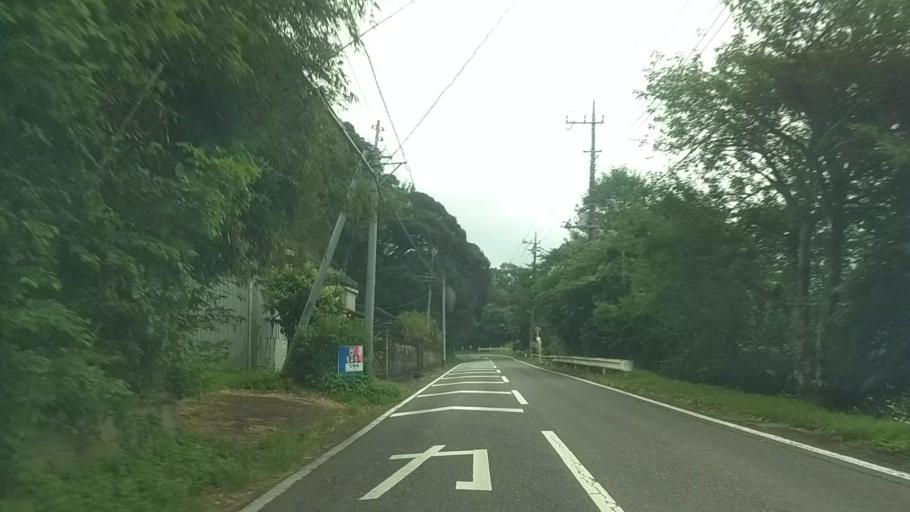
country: JP
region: Chiba
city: Kimitsu
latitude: 35.2323
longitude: 140.0047
